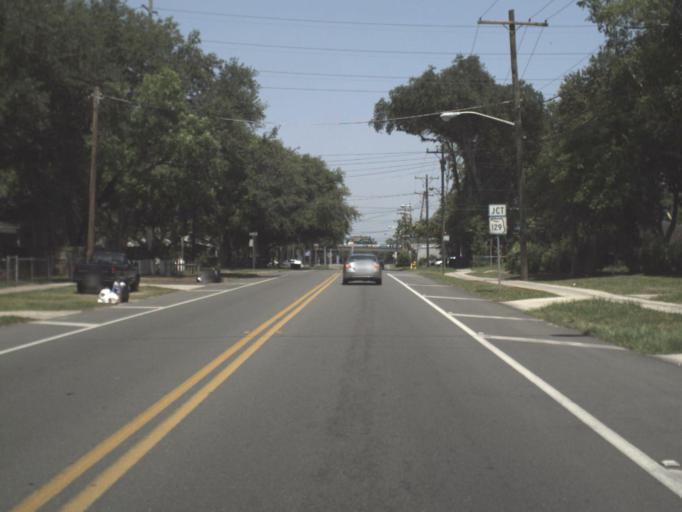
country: US
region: Florida
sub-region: Duval County
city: Jacksonville
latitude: 30.3133
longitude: -81.7083
